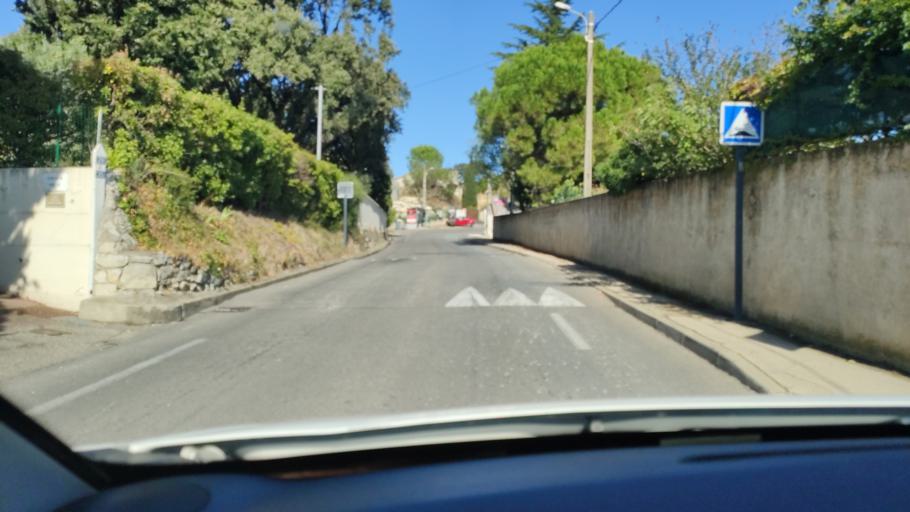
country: FR
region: Languedoc-Roussillon
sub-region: Departement du Gard
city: Villeneuve-les-Avignon
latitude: 43.9756
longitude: 4.7892
